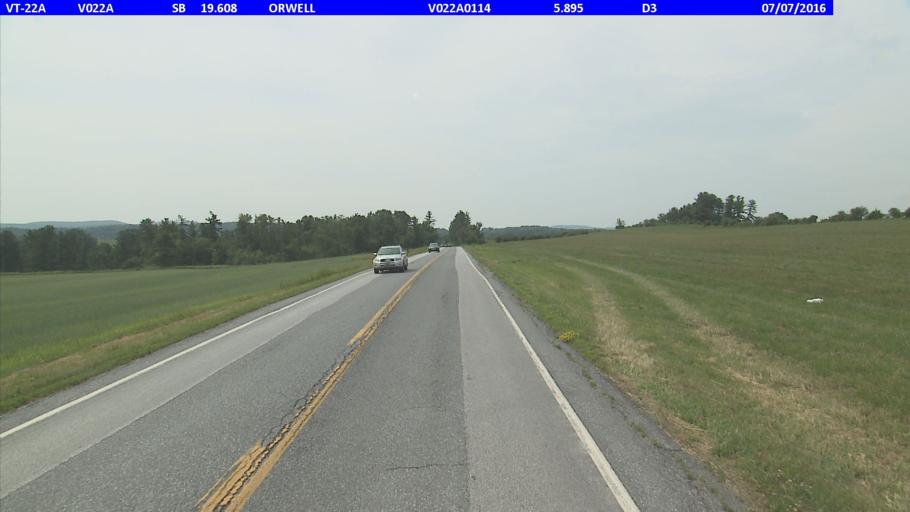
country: US
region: New York
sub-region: Essex County
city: Ticonderoga
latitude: 43.8417
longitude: -73.3100
